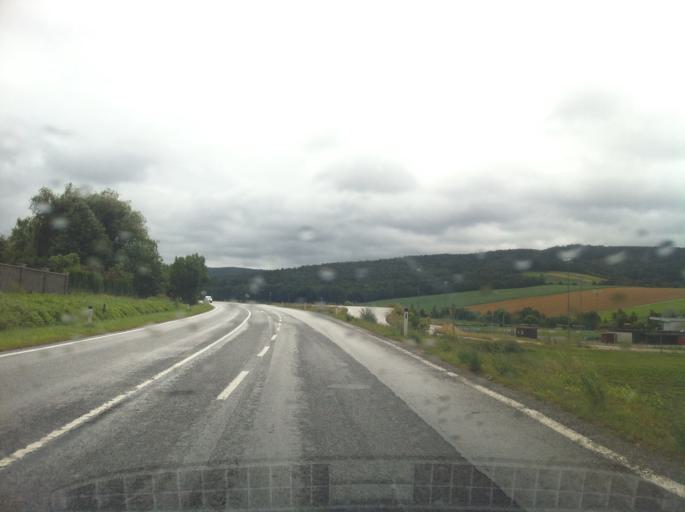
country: AT
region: Lower Austria
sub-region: Politischer Bezirk Tulln
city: Sieghartskirchen
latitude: 48.2530
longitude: 16.0235
